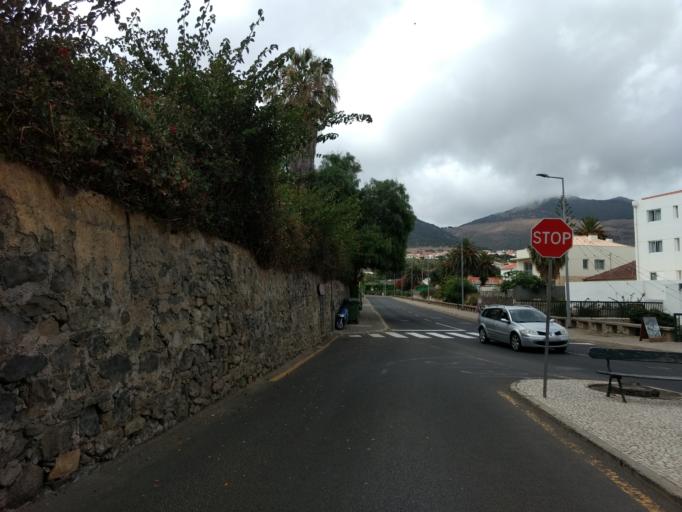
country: PT
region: Madeira
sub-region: Porto Santo
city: Vila de Porto Santo
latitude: 33.0606
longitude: -16.3350
